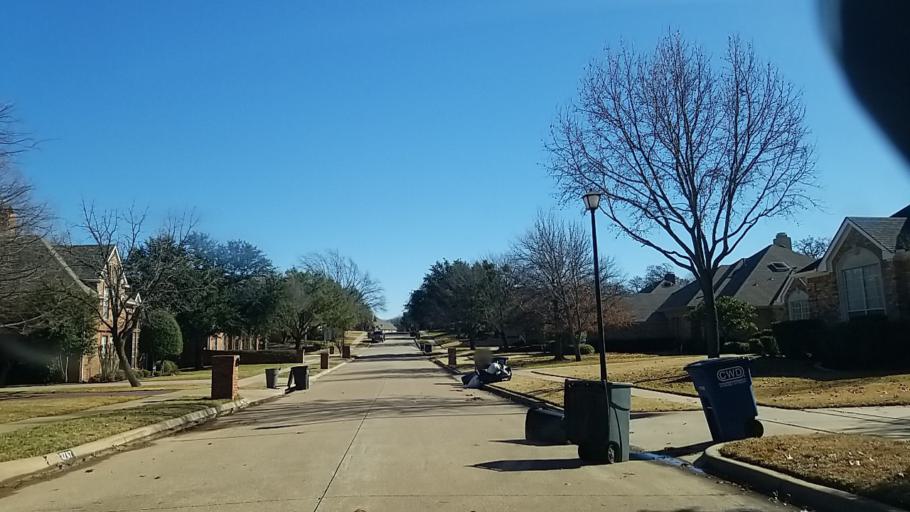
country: US
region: Texas
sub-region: Denton County
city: Corinth
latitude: 33.1574
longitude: -97.0837
